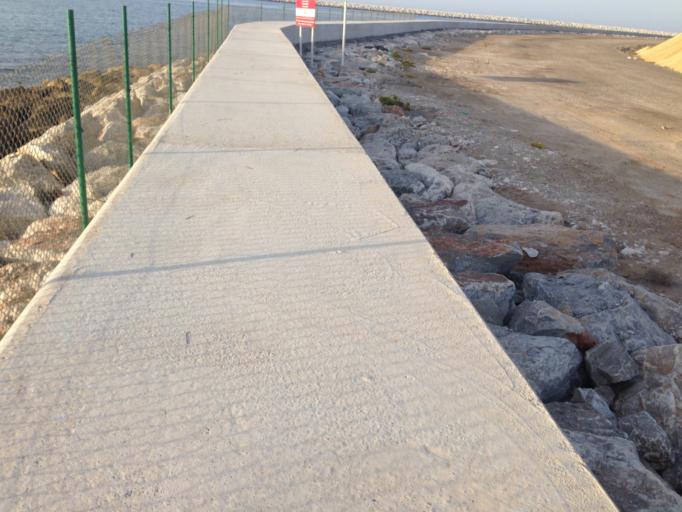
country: OM
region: Muhafazat Masqat
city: As Sib al Jadidah
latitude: 23.6333
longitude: 58.2630
